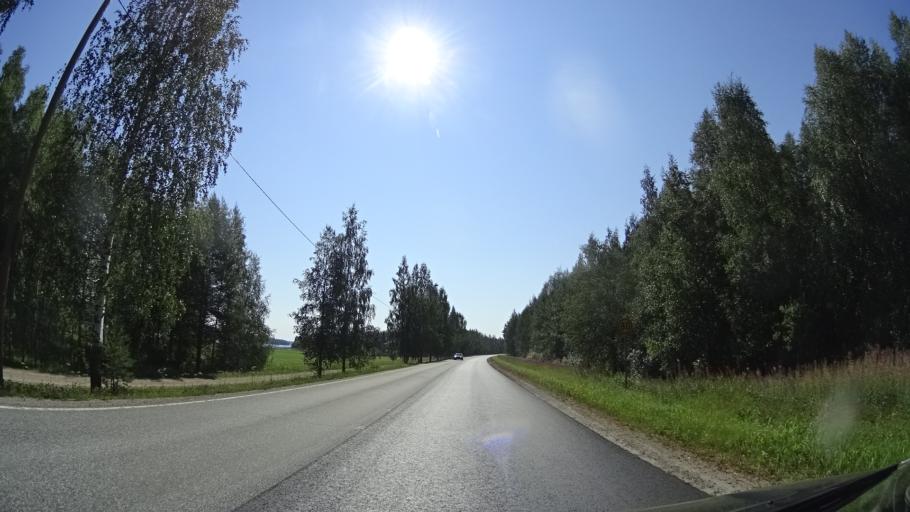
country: FI
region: North Karelia
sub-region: Joensuu
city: Juuka
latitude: 63.2451
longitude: 29.2718
